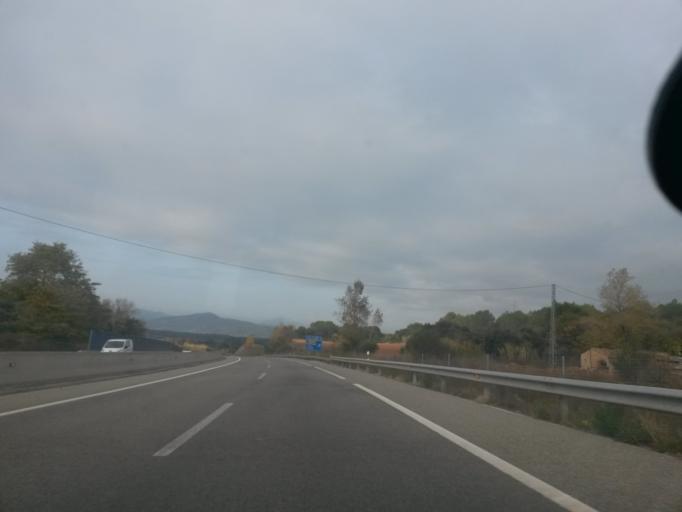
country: ES
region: Catalonia
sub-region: Provincia de Girona
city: Sant Ferriol
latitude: 42.2108
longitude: 2.6707
